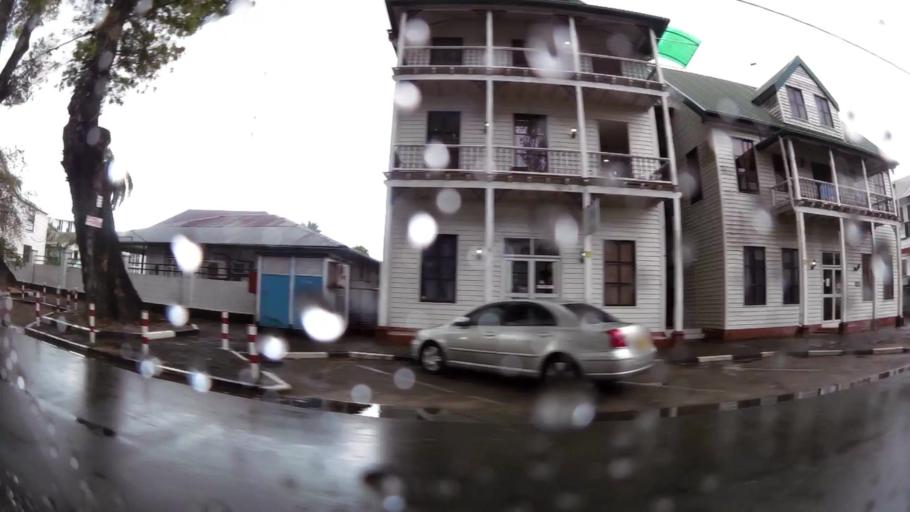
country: SR
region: Paramaribo
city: Paramaribo
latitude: 5.8284
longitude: -55.1562
